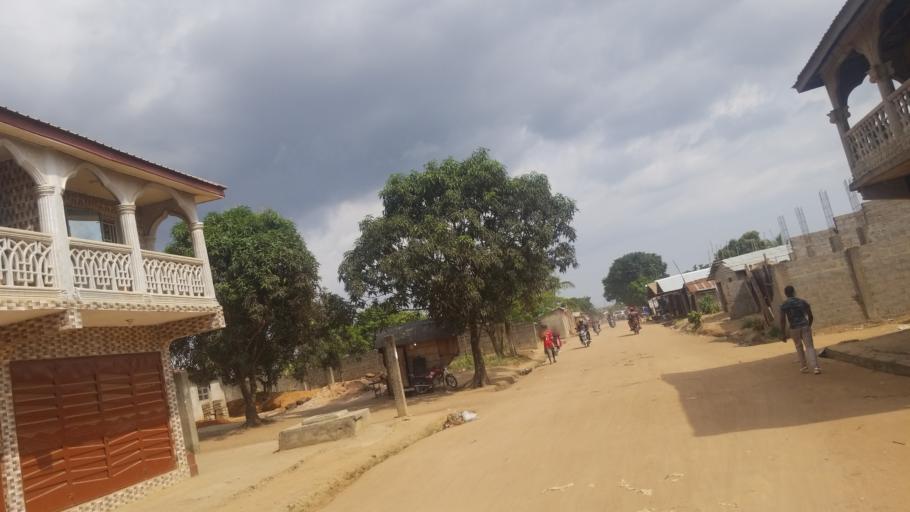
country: SL
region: Western Area
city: Waterloo
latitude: 8.3362
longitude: -13.0491
